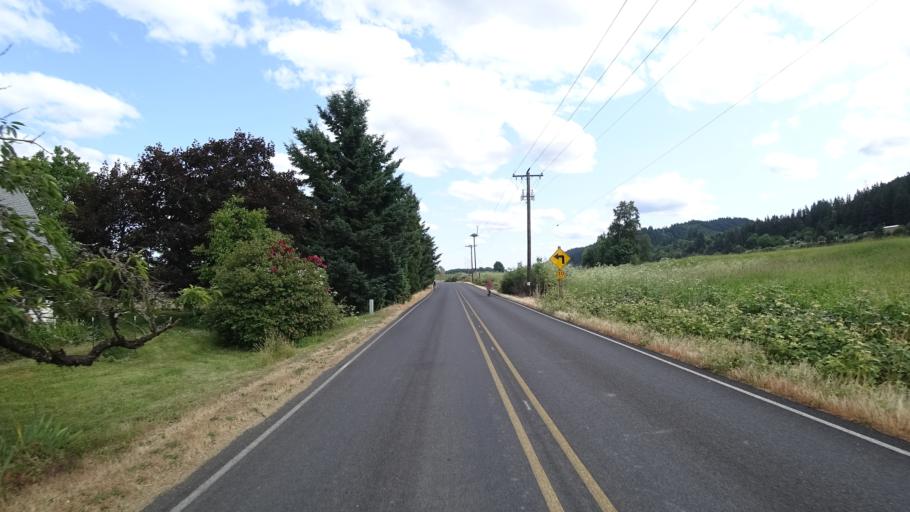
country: US
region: Oregon
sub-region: Washington County
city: Bethany
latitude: 45.6273
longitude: -122.8131
